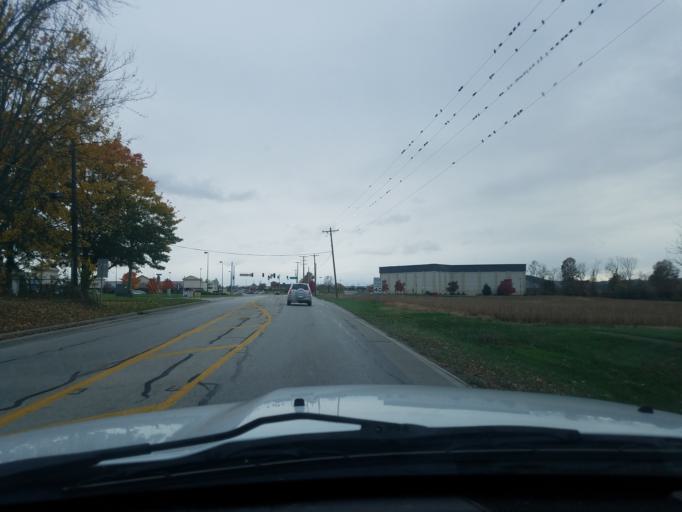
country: US
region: Indiana
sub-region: Clark County
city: Sellersburg
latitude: 38.3551
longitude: -85.7909
